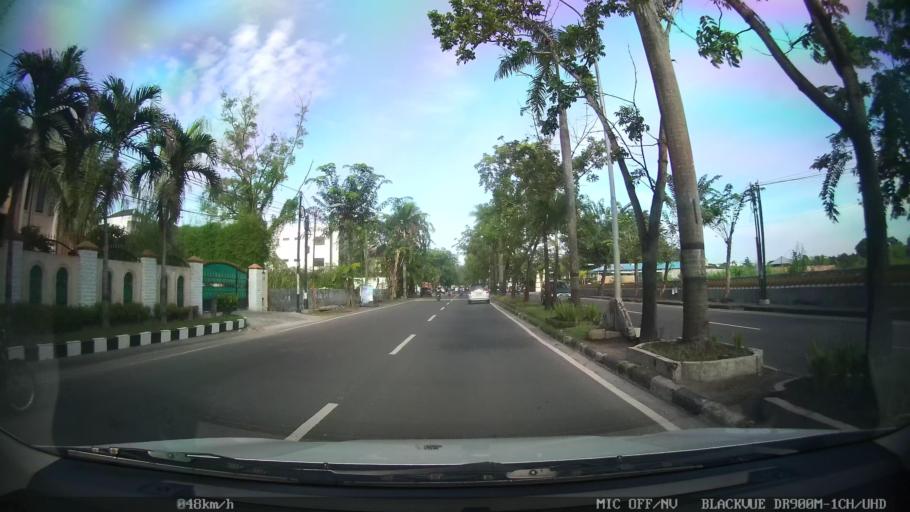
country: ID
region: North Sumatra
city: Medan
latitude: 3.6079
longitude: 98.6557
